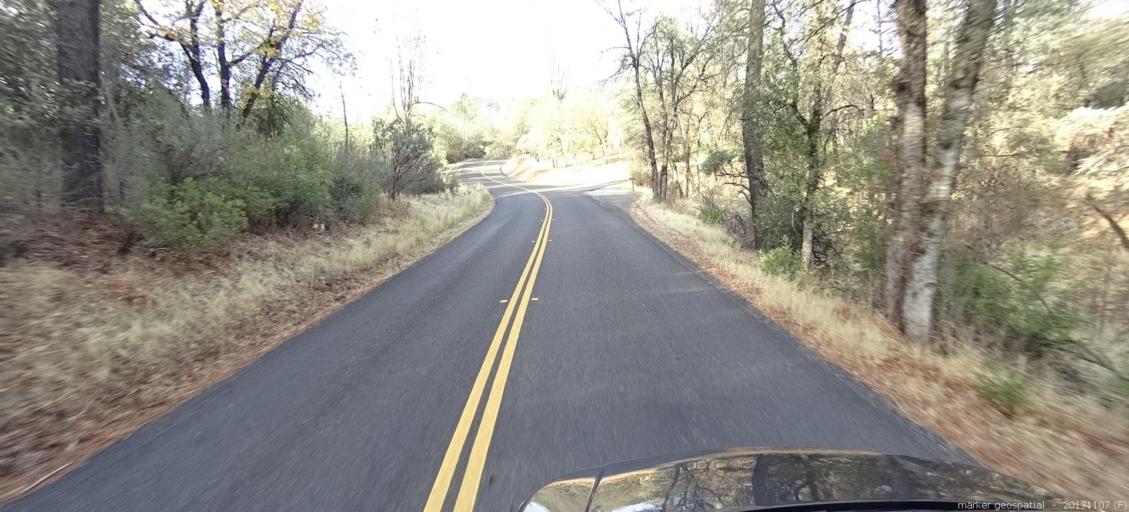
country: US
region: California
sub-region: Shasta County
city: Shasta
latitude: 40.5719
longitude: -122.4637
